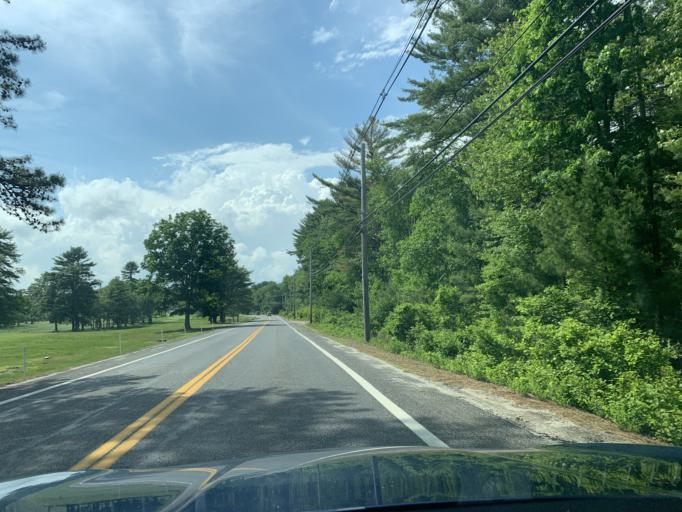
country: US
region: Rhode Island
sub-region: Kent County
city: West Greenwich
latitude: 41.6699
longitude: -71.6272
